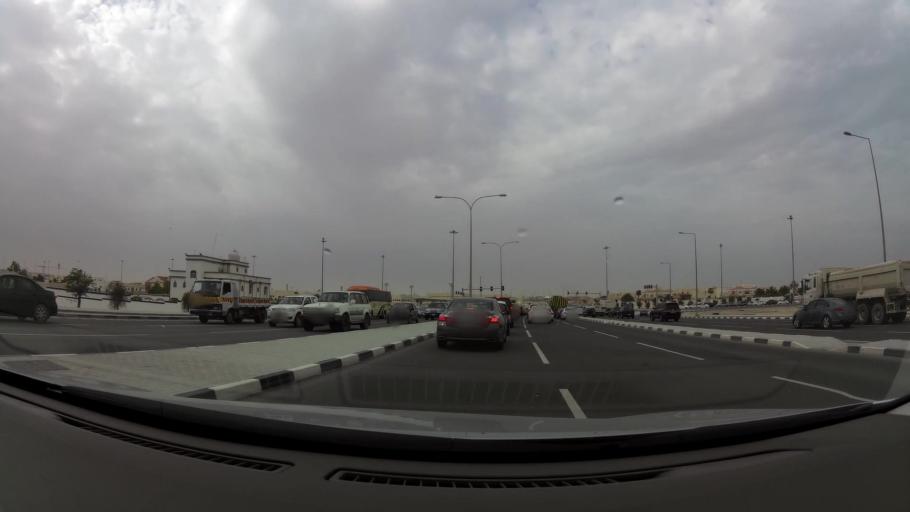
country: QA
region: Baladiyat ar Rayyan
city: Ar Rayyan
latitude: 25.3478
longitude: 51.4790
